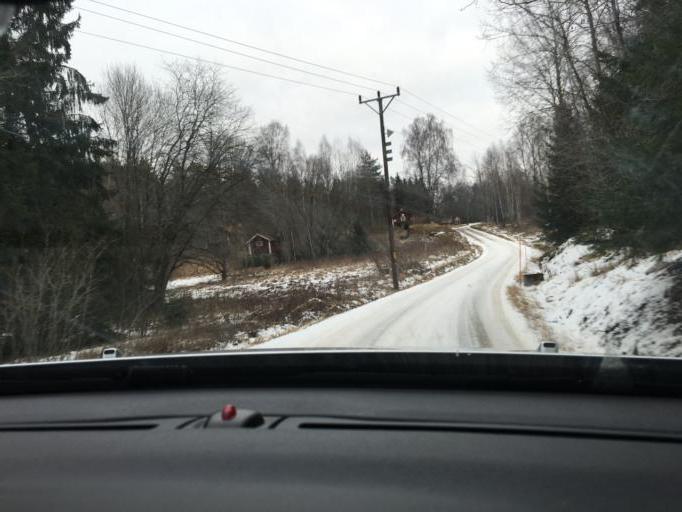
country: SE
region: Soedermanland
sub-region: Katrineholms Kommun
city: Katrineholm
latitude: 58.9984
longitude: 16.2961
